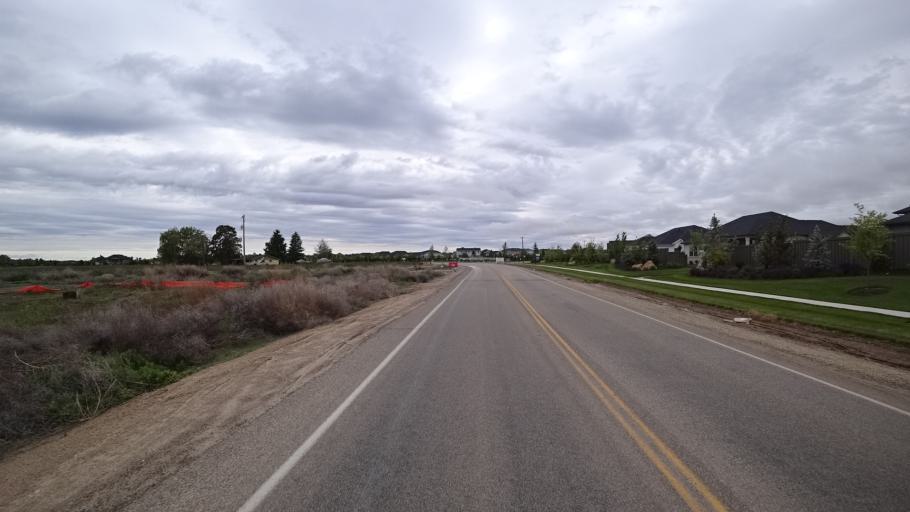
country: US
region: Idaho
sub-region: Ada County
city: Eagle
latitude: 43.7067
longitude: -116.4225
